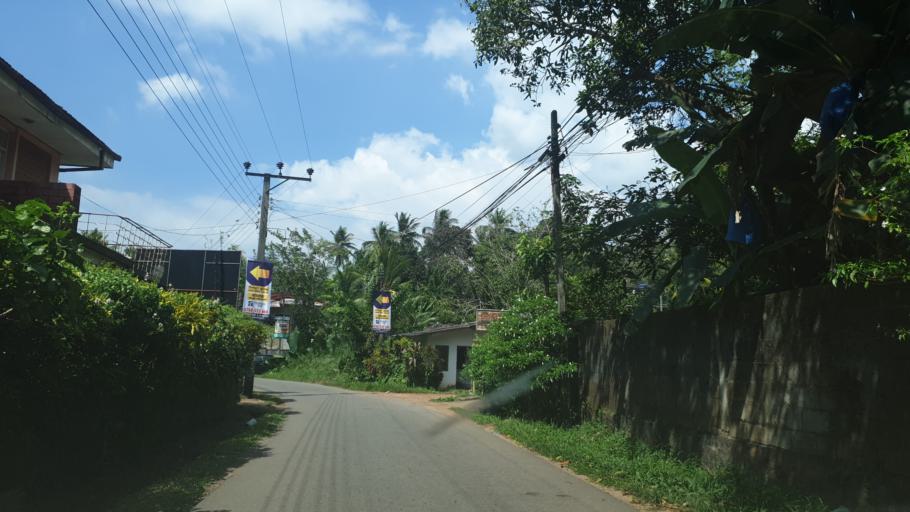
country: LK
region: Western
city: Horana South
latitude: 6.7087
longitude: 79.9831
